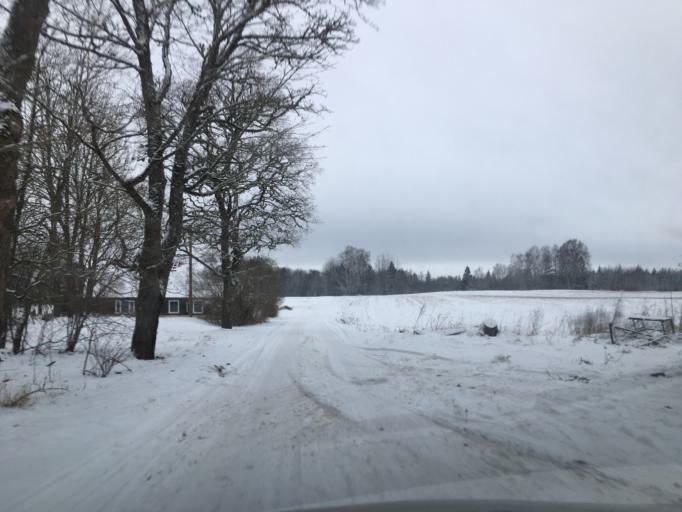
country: EE
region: Tartu
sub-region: Puhja vald
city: Puhja
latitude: 58.1922
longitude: 26.2031
